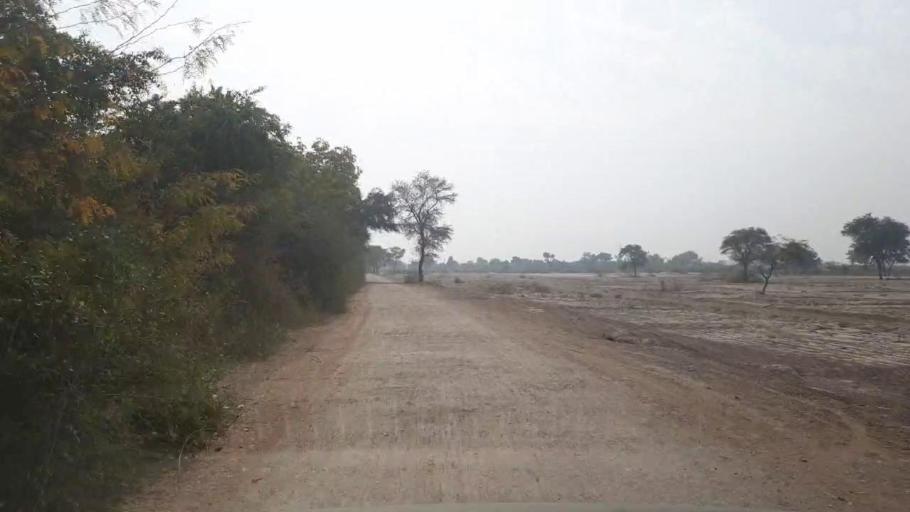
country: PK
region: Sindh
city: Hala
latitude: 25.7776
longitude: 68.4360
